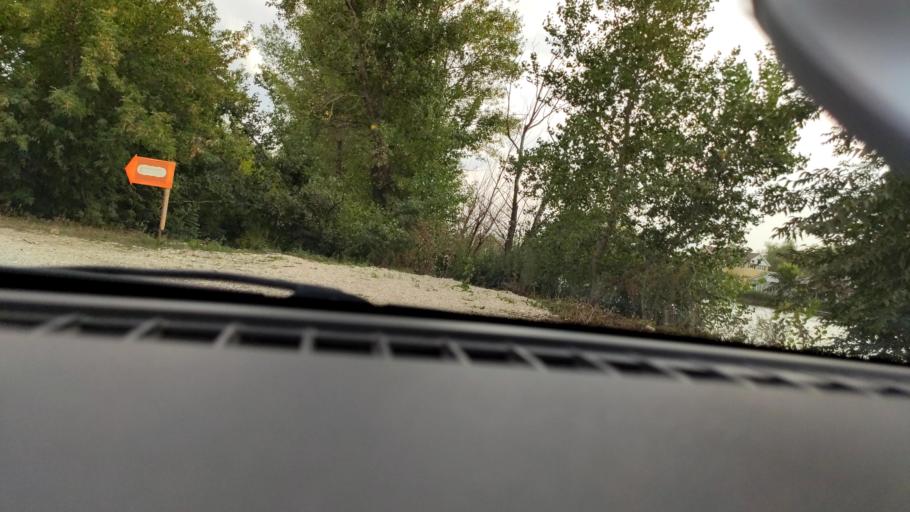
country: RU
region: Samara
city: Samara
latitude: 53.1465
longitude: 50.0882
